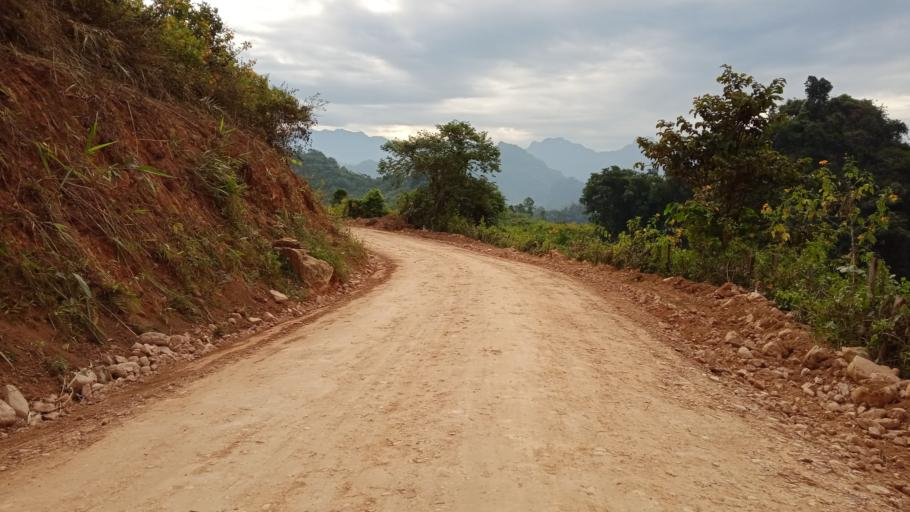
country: LA
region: Xiangkhoang
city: Phonsavan
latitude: 19.1177
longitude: 102.9172
